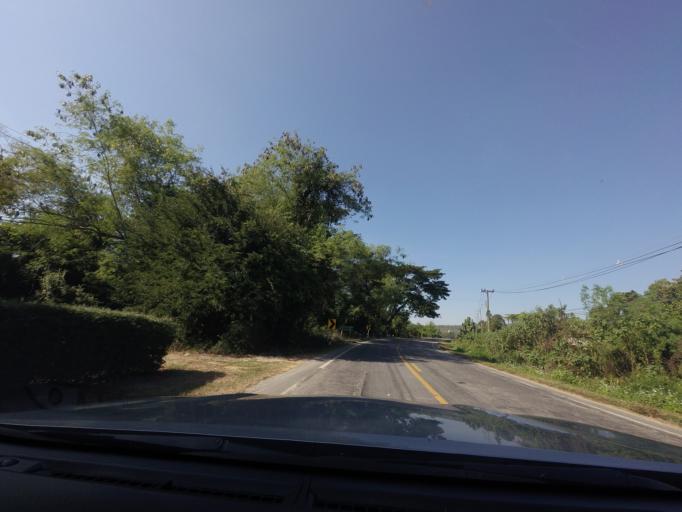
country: TH
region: Sukhothai
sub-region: Amphoe Si Satchanalai
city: Si Satchanalai
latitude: 17.6263
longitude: 99.7013
